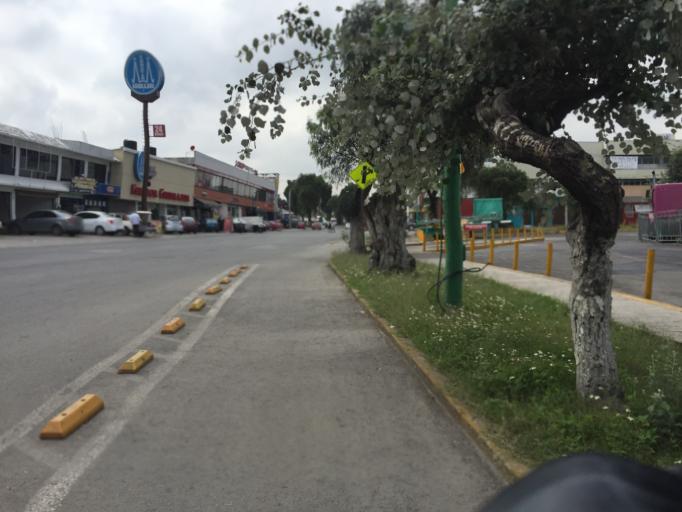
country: MX
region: Mexico
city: Cuautitlan Izcalli
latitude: 19.6637
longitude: -99.2087
